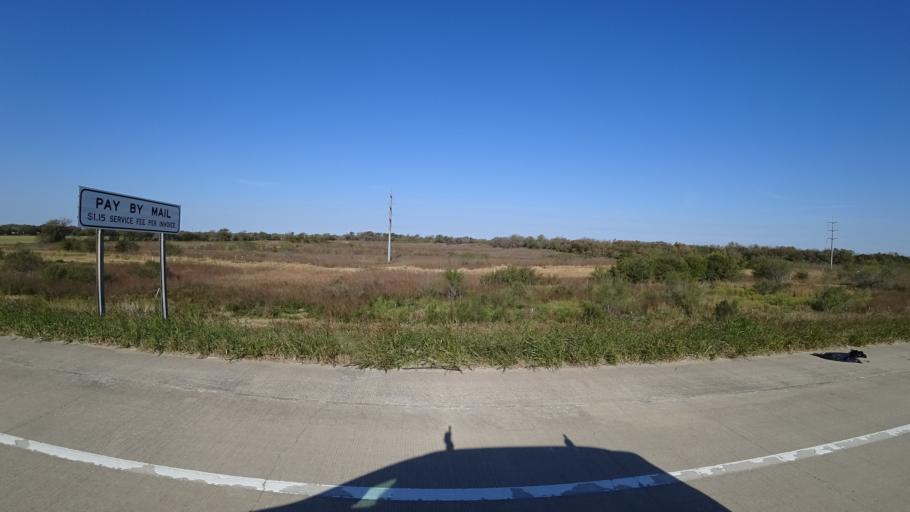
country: US
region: Texas
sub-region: Travis County
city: Garfield
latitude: 30.1719
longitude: -97.6436
